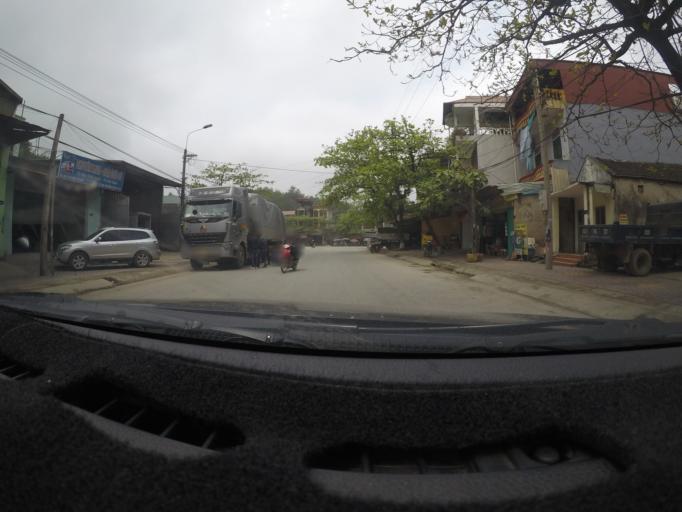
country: VN
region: Yen Bai
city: Yen Bai
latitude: 21.7394
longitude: 104.9484
